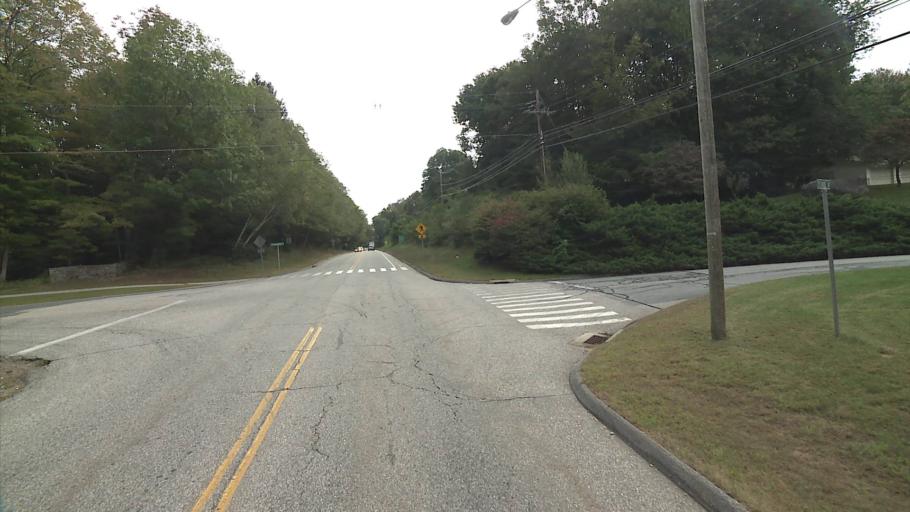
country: US
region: Connecticut
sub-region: Tolland County
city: Storrs
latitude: 41.7949
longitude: -72.2560
